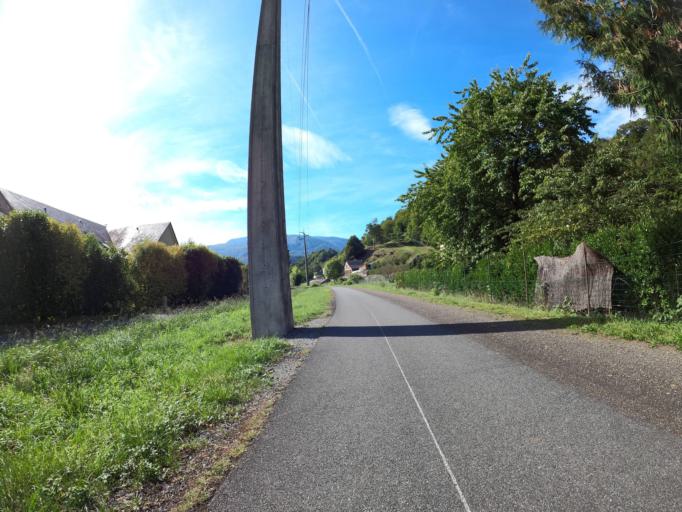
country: FR
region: Midi-Pyrenees
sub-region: Departement des Hautes-Pyrenees
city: Argeles-Gazost
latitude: 43.0186
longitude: -0.0963
